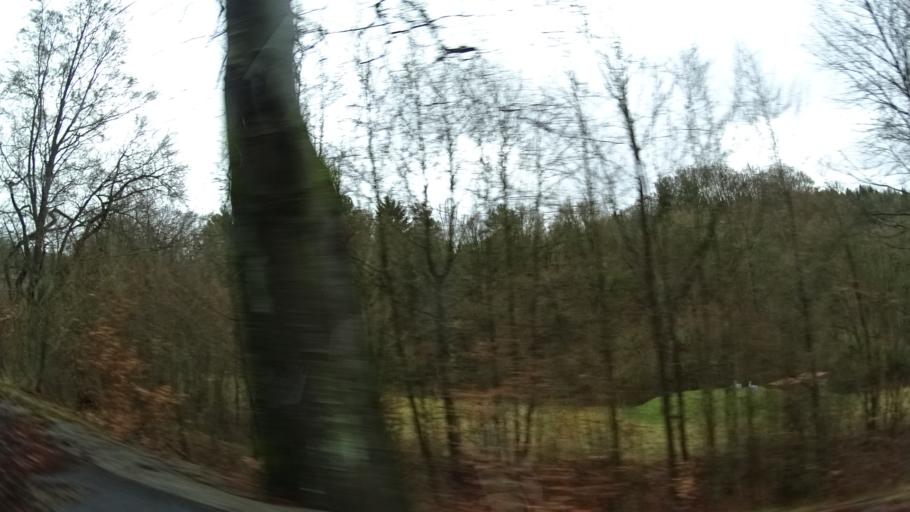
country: DE
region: Thuringia
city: Unterweid
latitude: 50.6096
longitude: 10.0687
